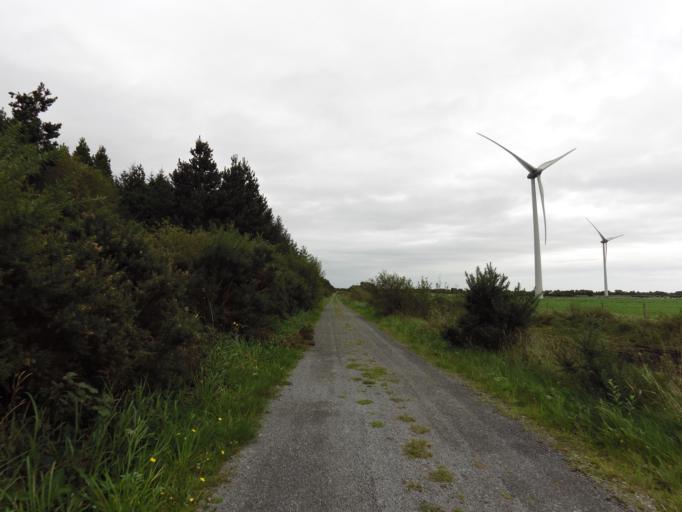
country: IE
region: Leinster
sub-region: Uibh Fhaili
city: Ferbane
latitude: 53.2320
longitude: -7.7724
